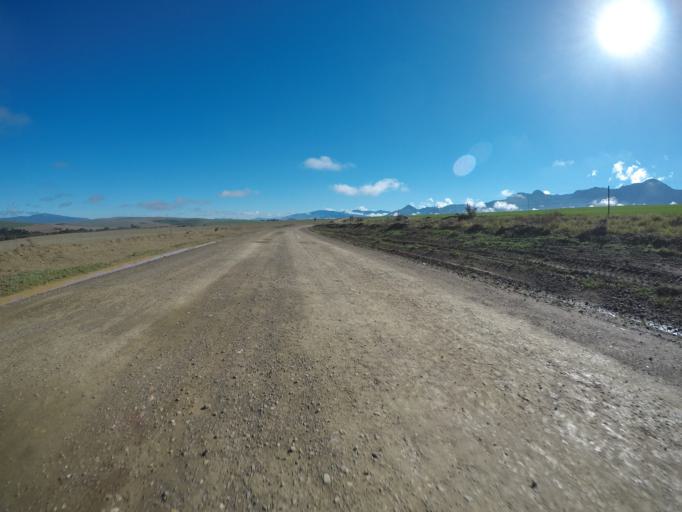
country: ZA
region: Western Cape
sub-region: Overberg District Municipality
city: Caledon
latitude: -34.1186
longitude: 19.7163
